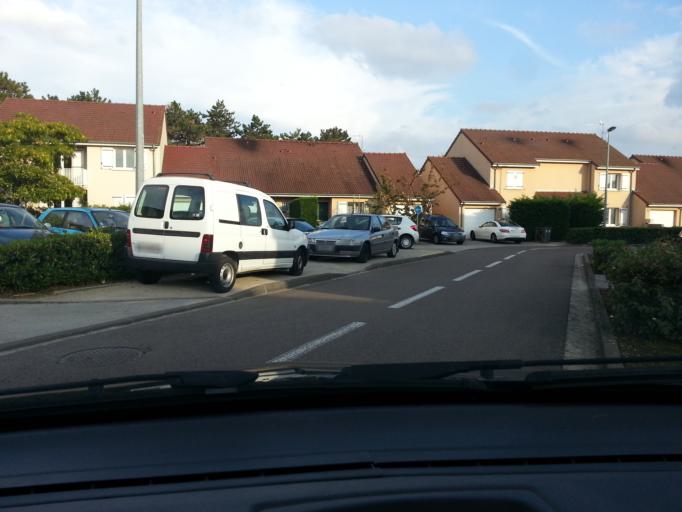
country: FR
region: Bourgogne
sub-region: Departement de Saone-et-Loire
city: Chatenoy-le-Royal
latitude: 46.7820
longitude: 4.8239
